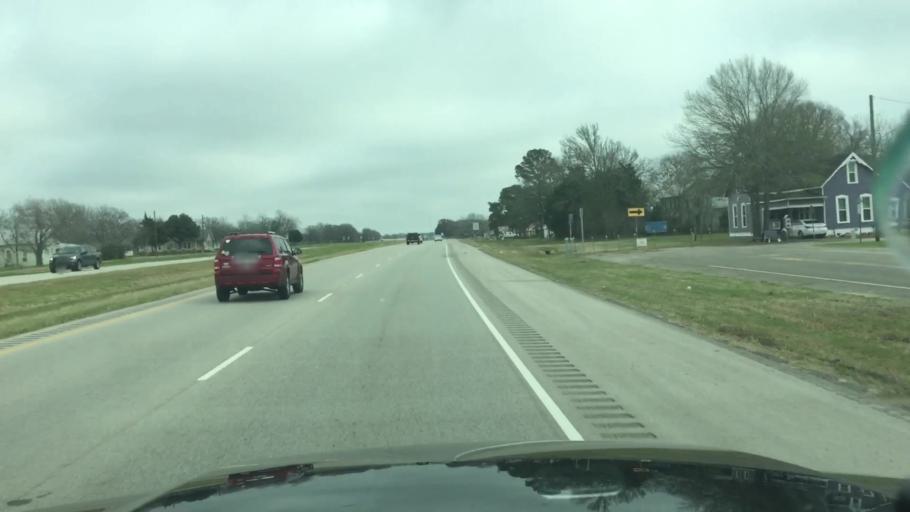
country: US
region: Texas
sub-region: Burleson County
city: Somerville
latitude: 30.1497
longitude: -96.6854
